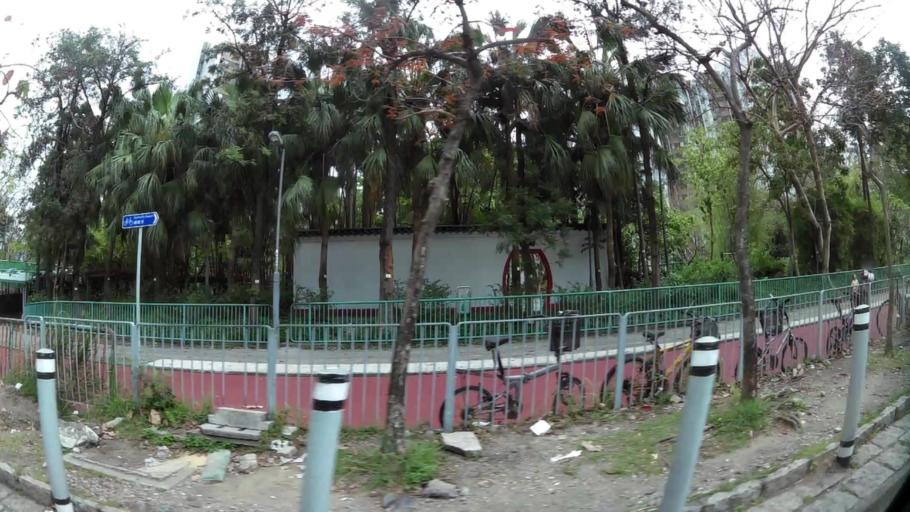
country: HK
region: Tuen Mun
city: Tuen Mun
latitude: 22.3785
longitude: 113.9623
